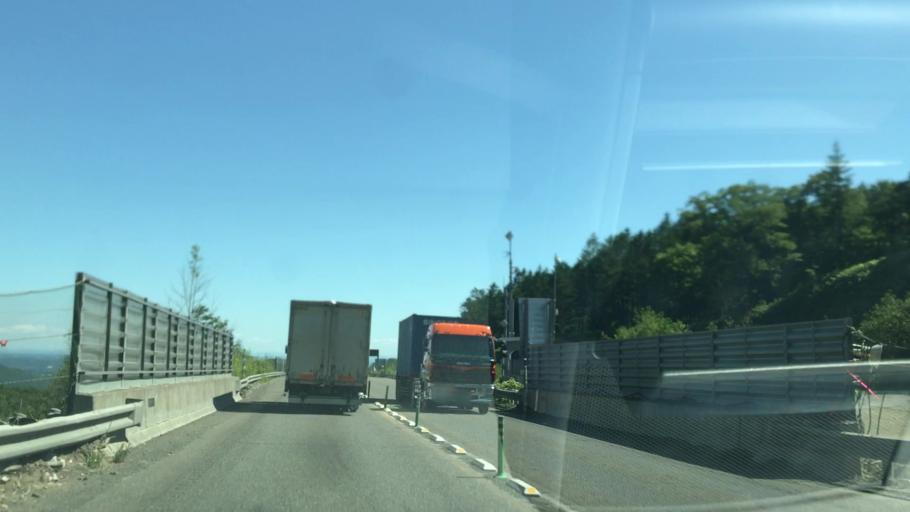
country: JP
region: Hokkaido
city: Shimo-furano
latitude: 43.0708
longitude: 142.7479
